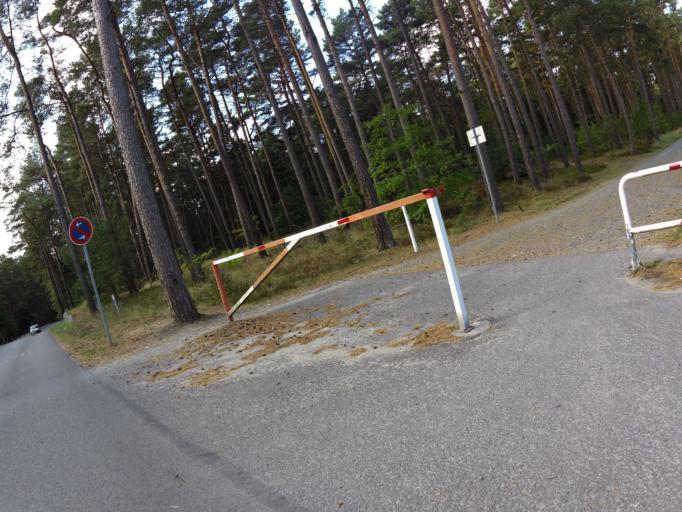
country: DE
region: Mecklenburg-Vorpommern
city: Ostseebad Zinnowitz
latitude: 54.0927
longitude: 13.8745
